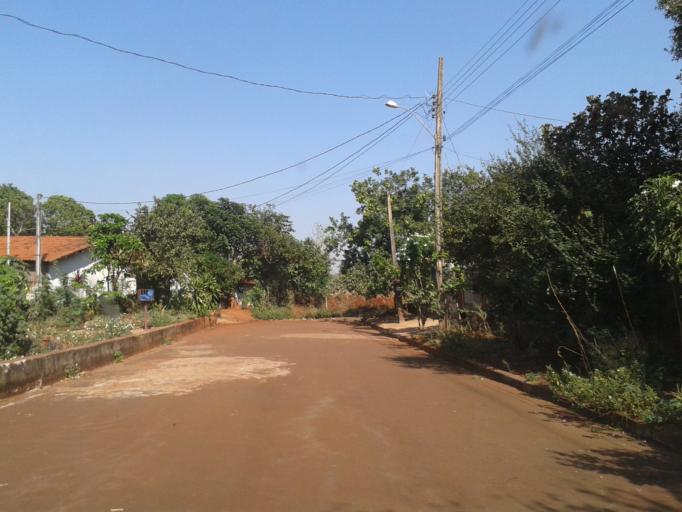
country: BR
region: Minas Gerais
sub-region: Ituiutaba
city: Ituiutaba
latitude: -18.9639
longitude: -49.4810
